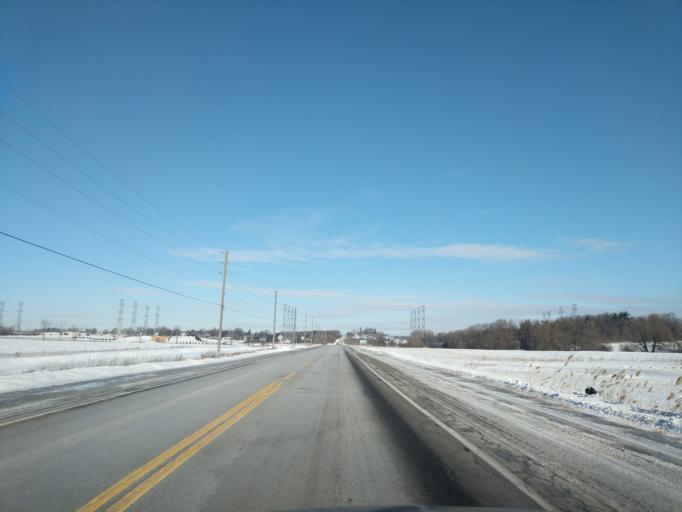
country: CA
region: Ontario
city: Pickering
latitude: 43.8393
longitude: -79.1464
